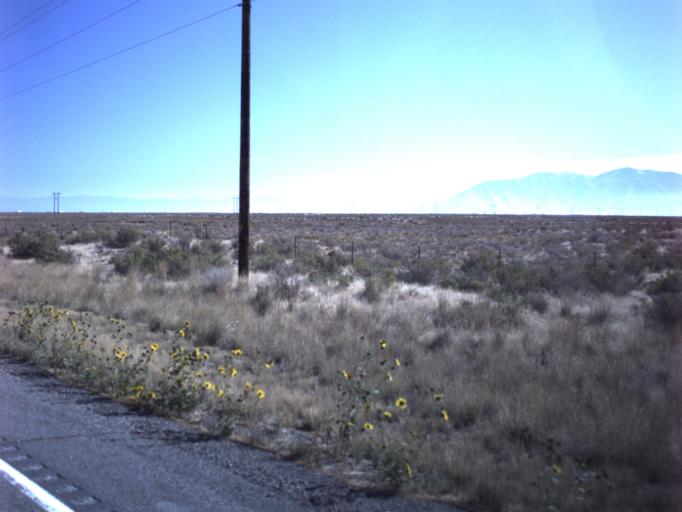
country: US
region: Utah
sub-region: Tooele County
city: Grantsville
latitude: 40.6887
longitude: -112.5392
